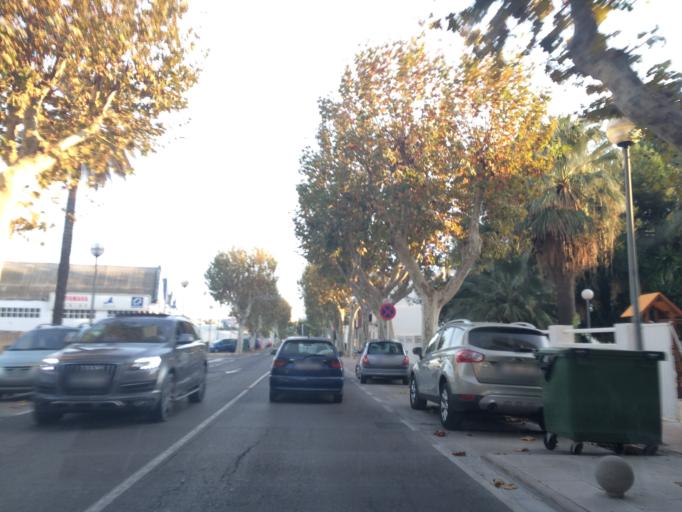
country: ES
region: Valencia
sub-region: Provincia de Alicante
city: Denia
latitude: 38.8405
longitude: 0.1135
